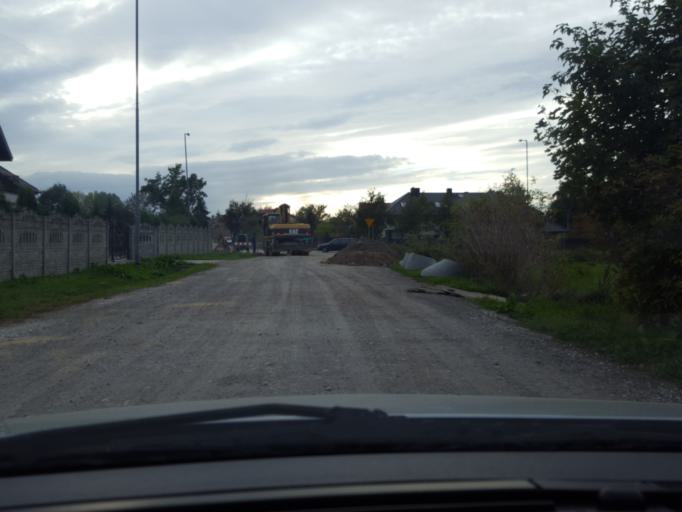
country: PL
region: Lodz Voivodeship
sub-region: Powiat brzezinski
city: Brzeziny
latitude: 51.7972
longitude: 19.7636
